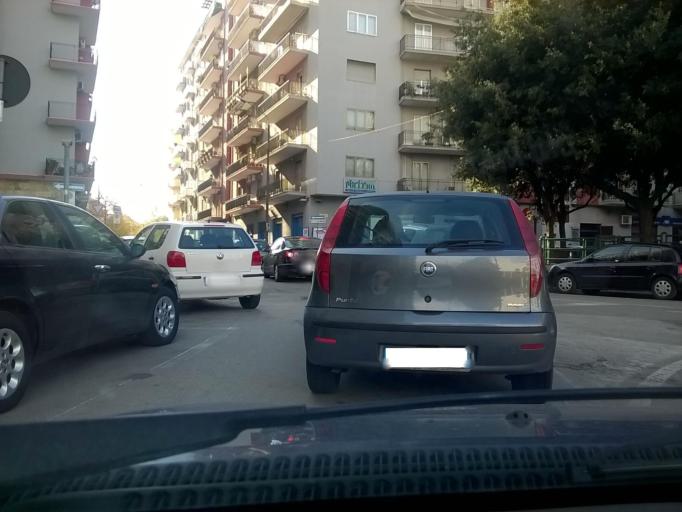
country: IT
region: Apulia
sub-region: Provincia di Taranto
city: Taranto
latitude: 40.4676
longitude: 17.2561
